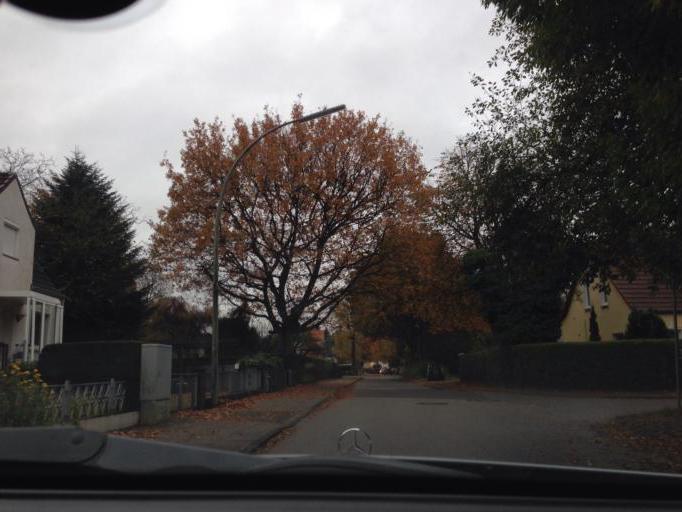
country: DE
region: Hamburg
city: Farmsen-Berne
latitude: 53.5894
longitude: 10.1379
